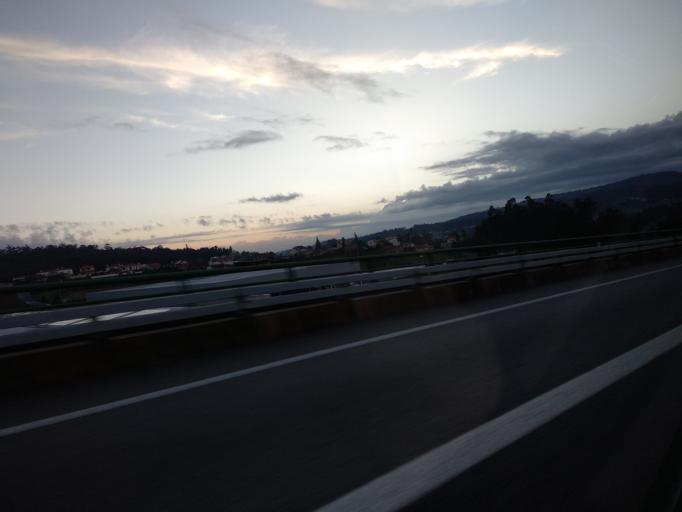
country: PT
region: Braga
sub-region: Braga
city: Oliveira
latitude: 41.4963
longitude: -8.4685
